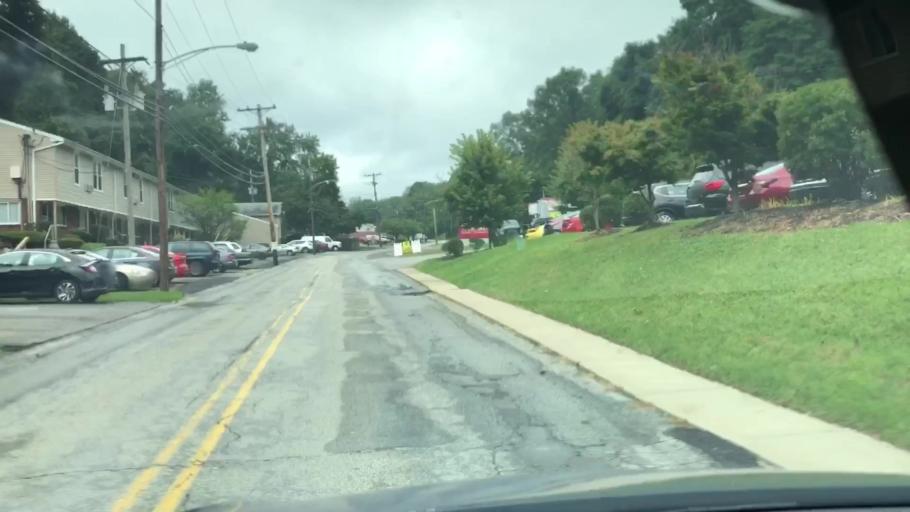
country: US
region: Pennsylvania
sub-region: Allegheny County
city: Castle Shannon
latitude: 40.3730
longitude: -80.0192
